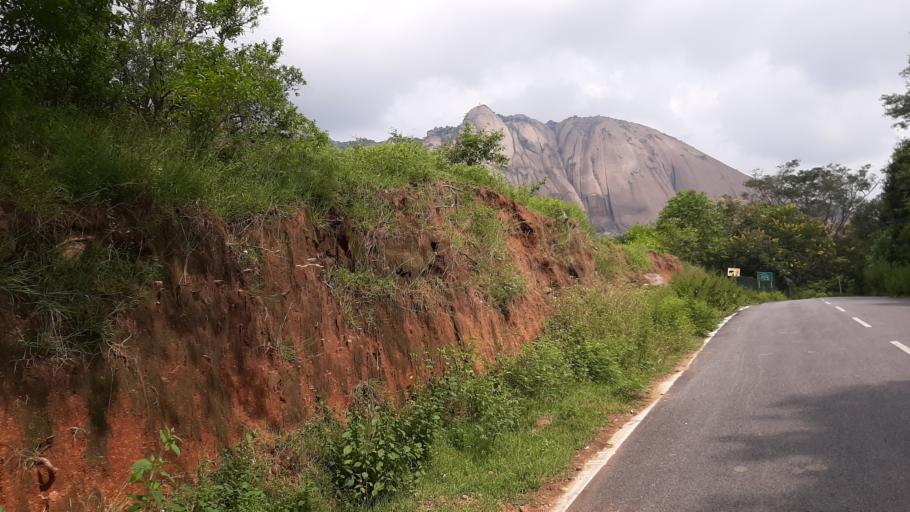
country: IN
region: Karnataka
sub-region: Ramanagara
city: Magadi
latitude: 12.9069
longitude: 77.2942
